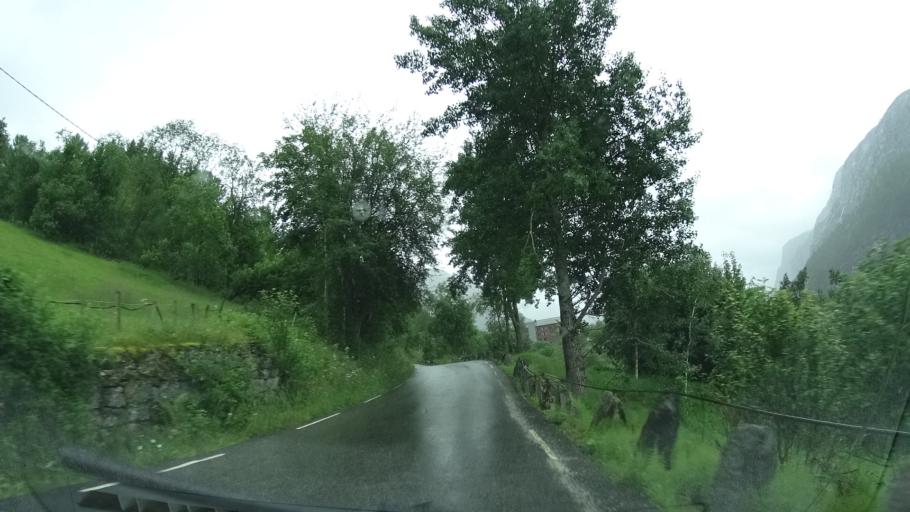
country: NO
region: Sogn og Fjordane
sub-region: Vik
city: Vik
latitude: 60.8329
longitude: 6.6780
